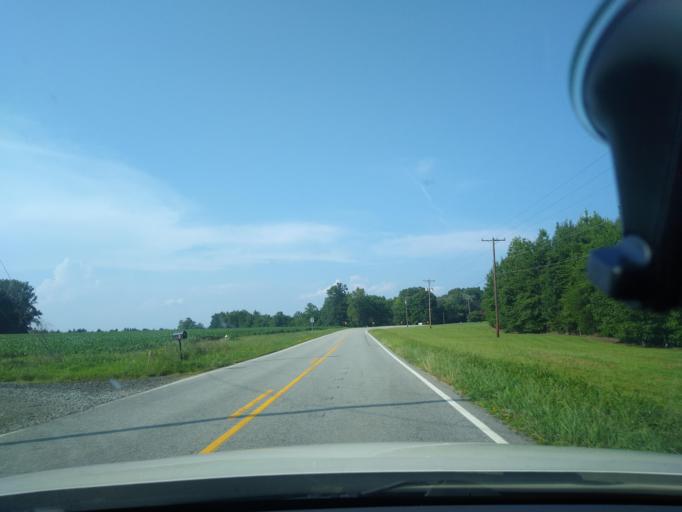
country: US
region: North Carolina
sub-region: Guilford County
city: McLeansville
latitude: 36.0923
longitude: -79.6778
